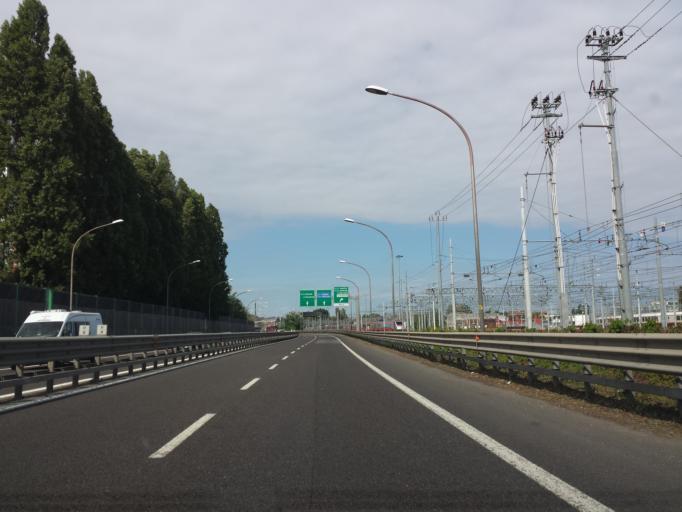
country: IT
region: Veneto
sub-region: Provincia di Venezia
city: Mestre
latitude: 45.4821
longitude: 12.2281
